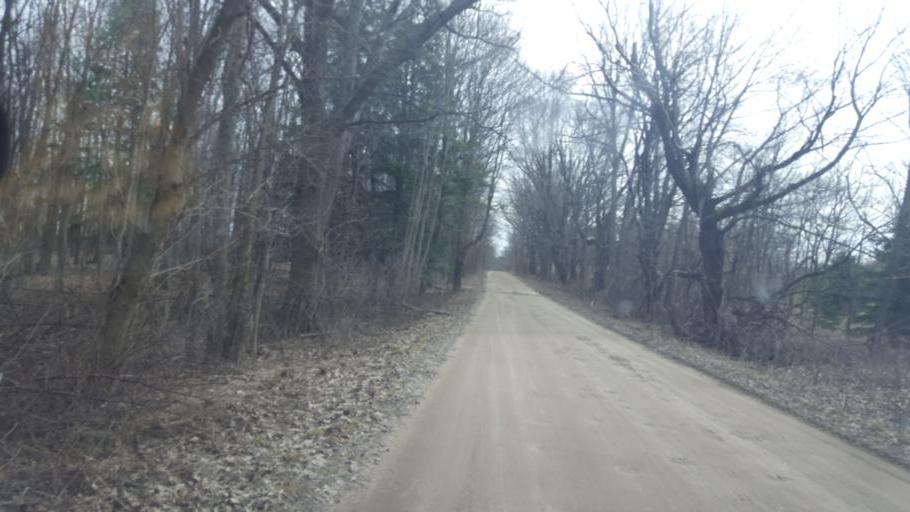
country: US
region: Michigan
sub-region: Isabella County
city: Lake Isabella
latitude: 43.6655
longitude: -85.1265
